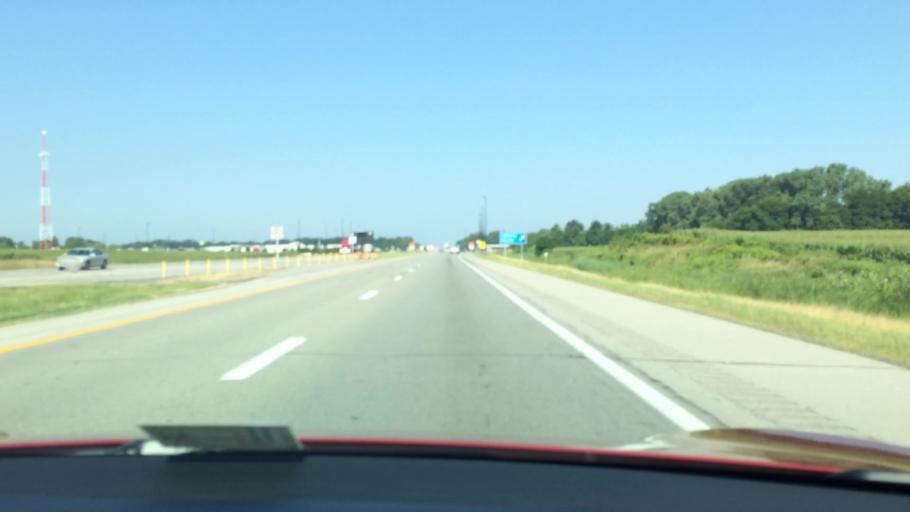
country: US
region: Ohio
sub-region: Williams County
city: West Unity
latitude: 41.6043
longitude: -84.3994
